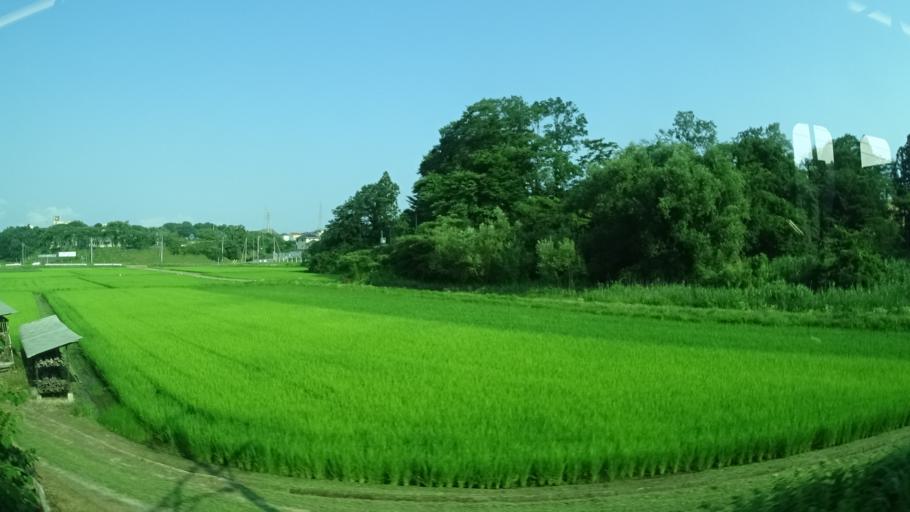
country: JP
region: Fukushima
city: Iwaki
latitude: 36.9520
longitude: 140.8415
